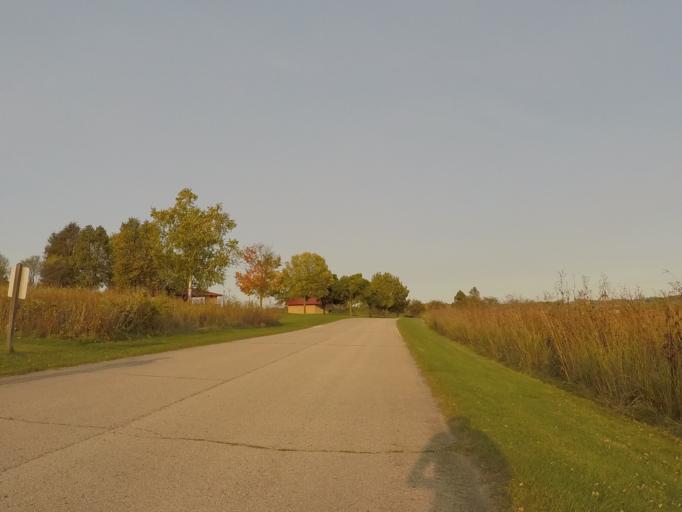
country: US
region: Wisconsin
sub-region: Dane County
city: Verona
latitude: 42.9974
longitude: -89.5212
